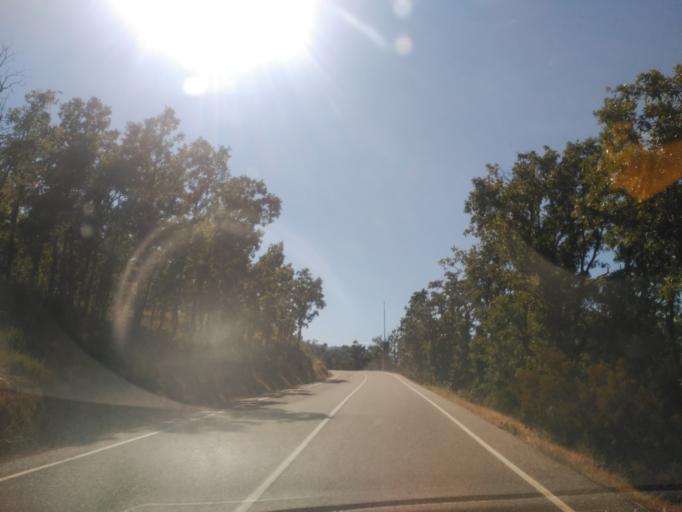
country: ES
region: Castille and Leon
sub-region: Provincia de Zamora
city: Galende
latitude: 42.1198
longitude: -6.7011
